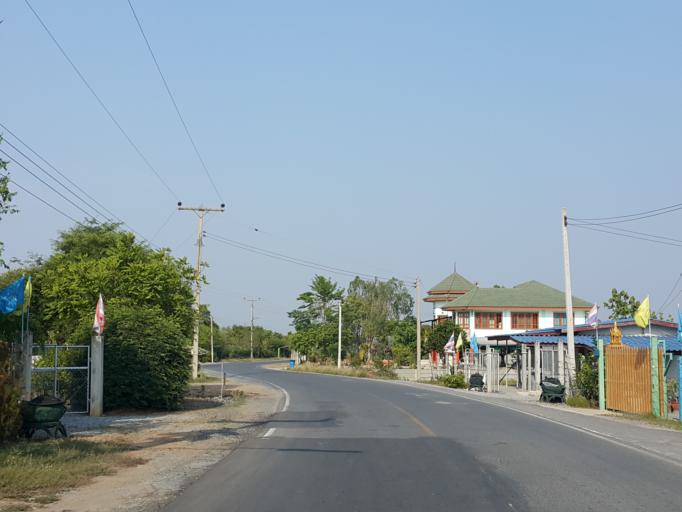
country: TH
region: Suphan Buri
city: Sam Chuk
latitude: 14.7451
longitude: 100.0418
